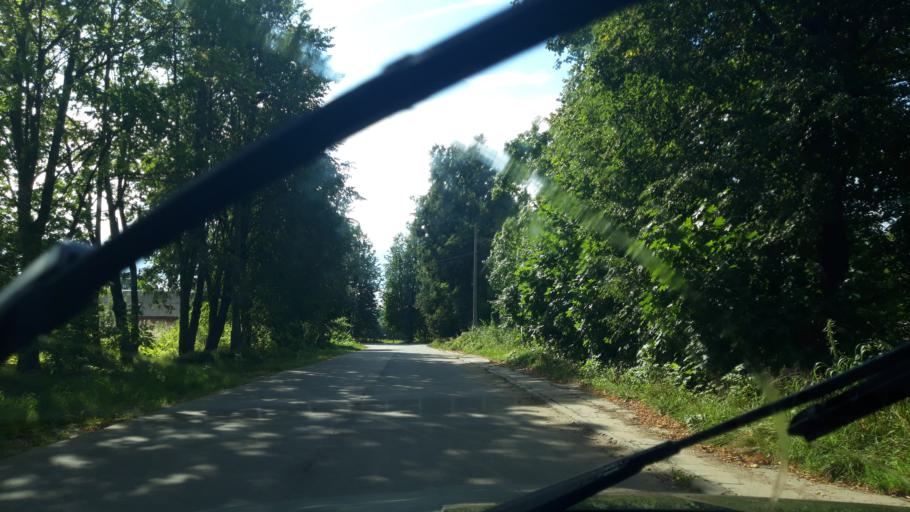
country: RU
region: Moskovskaya
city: Chashnikovo
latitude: 56.0350
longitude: 37.1700
